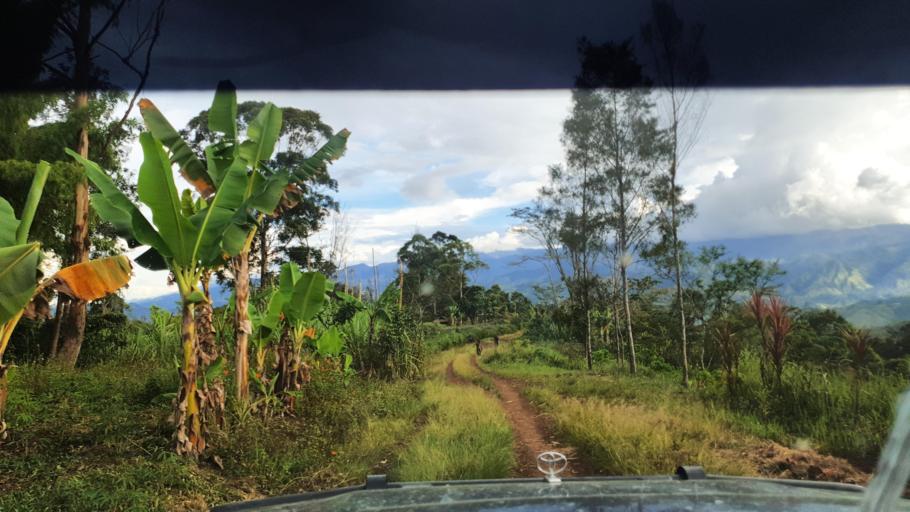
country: PG
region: Jiwaka
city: Minj
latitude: -5.9151
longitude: 144.8202
